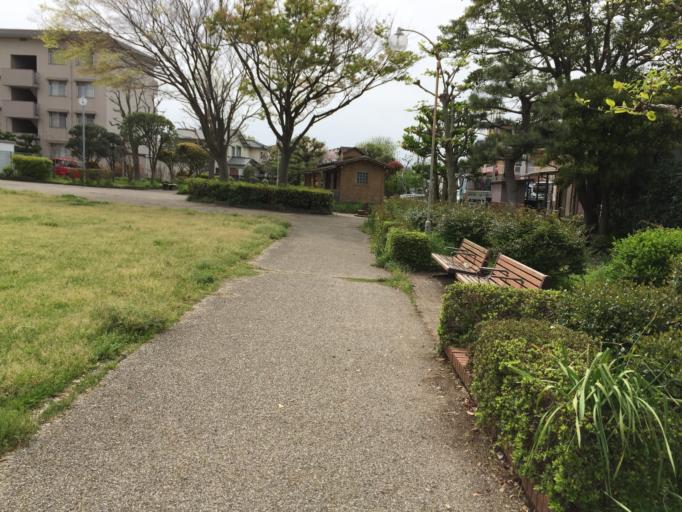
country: JP
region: Shizuoka
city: Numazu
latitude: 35.0874
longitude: 138.8573
